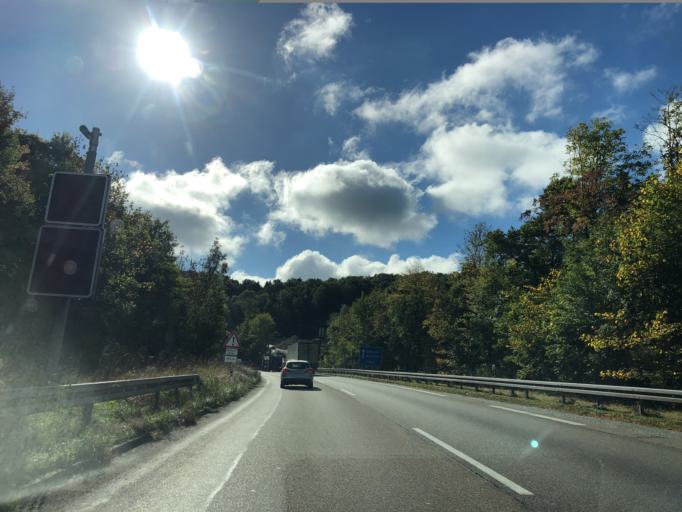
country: DE
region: Baden-Wuerttemberg
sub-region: Regierungsbezirk Stuttgart
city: Wiesensteig
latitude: 48.5523
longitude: 9.6331
